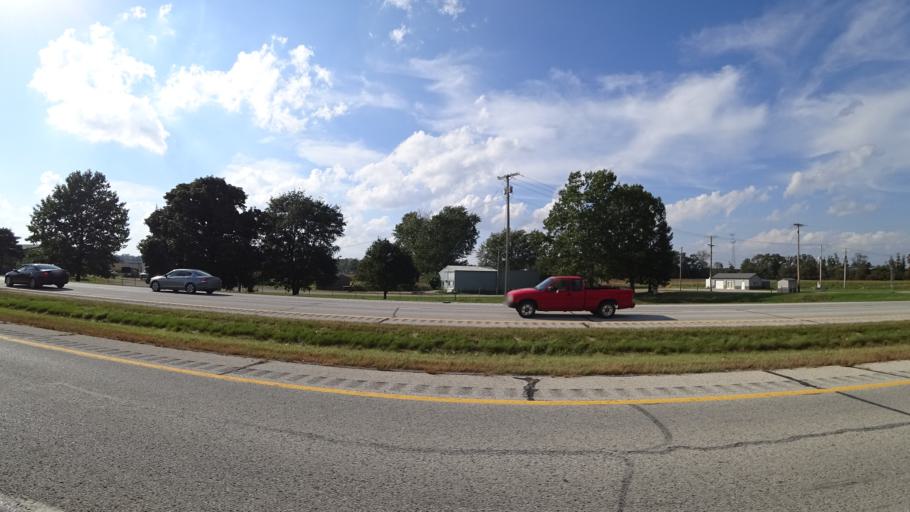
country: US
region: Michigan
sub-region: Saint Joseph County
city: Three Rivers
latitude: 41.9686
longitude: -85.6374
